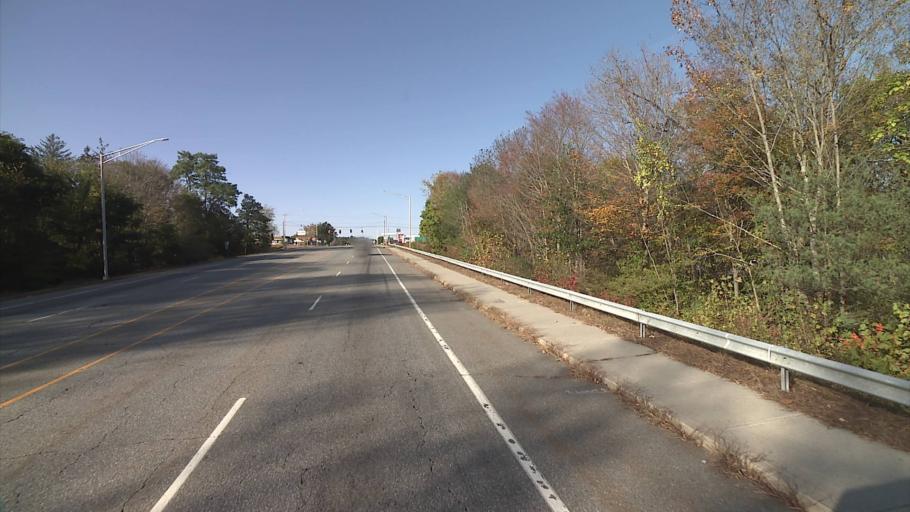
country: US
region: Connecticut
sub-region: Windham County
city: East Brooklyn
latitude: 41.8006
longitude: -71.8967
